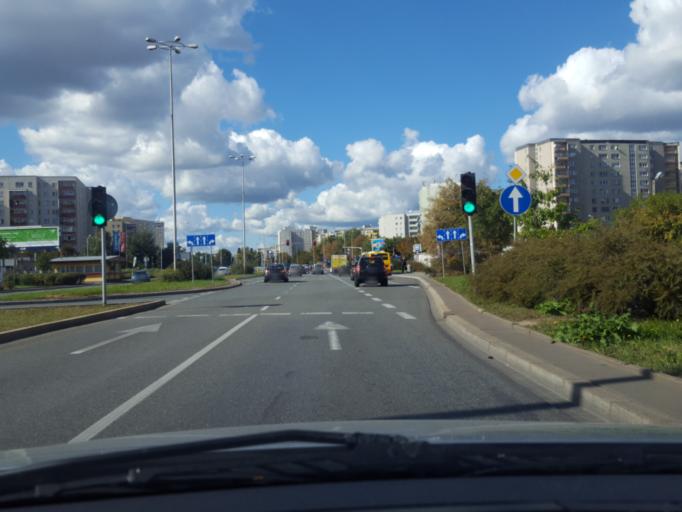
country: PL
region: Masovian Voivodeship
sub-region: Warszawa
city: Praga Poludnie
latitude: 52.2224
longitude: 21.1033
